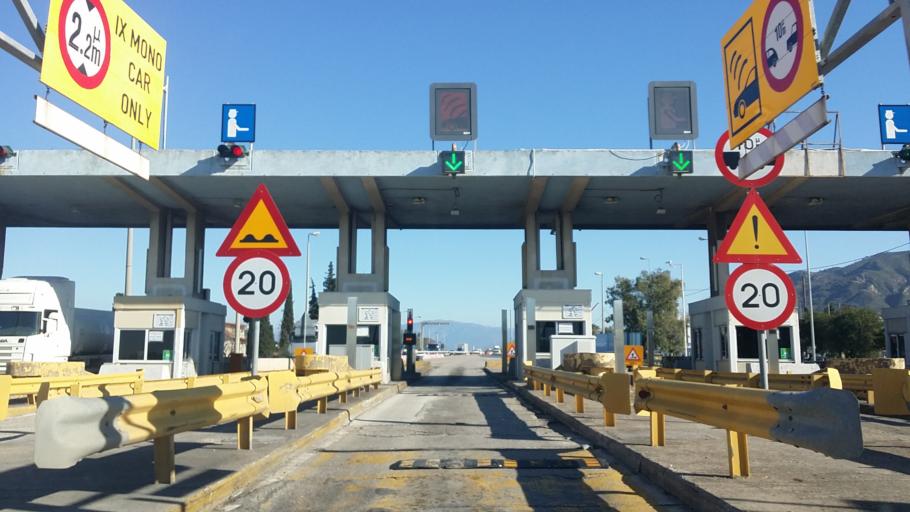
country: GR
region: West Greece
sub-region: Nomos Achaias
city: Rio
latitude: 38.3031
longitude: 21.8013
